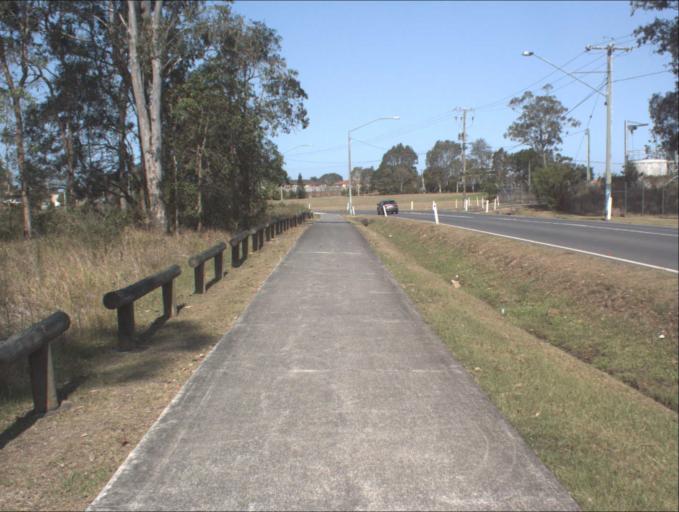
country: AU
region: Queensland
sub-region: Logan
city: Beenleigh
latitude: -27.6916
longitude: 153.1837
